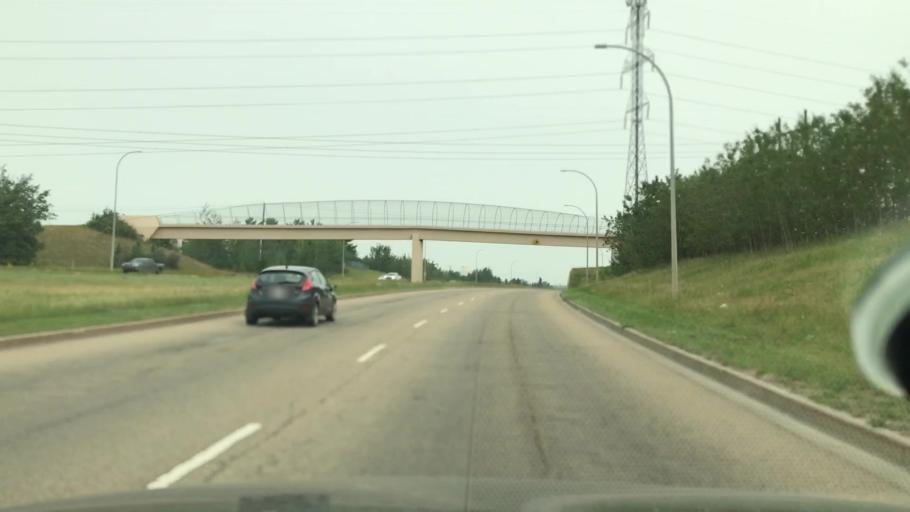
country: CA
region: Alberta
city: Edmonton
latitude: 53.4605
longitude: -113.5875
